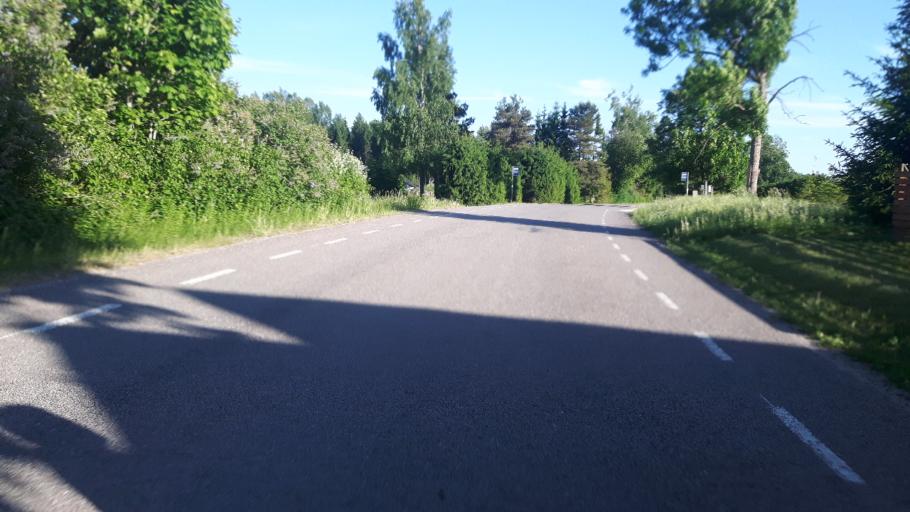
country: EE
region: Raplamaa
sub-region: Kehtna vald
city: Kehtna
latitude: 58.8984
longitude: 24.8797
